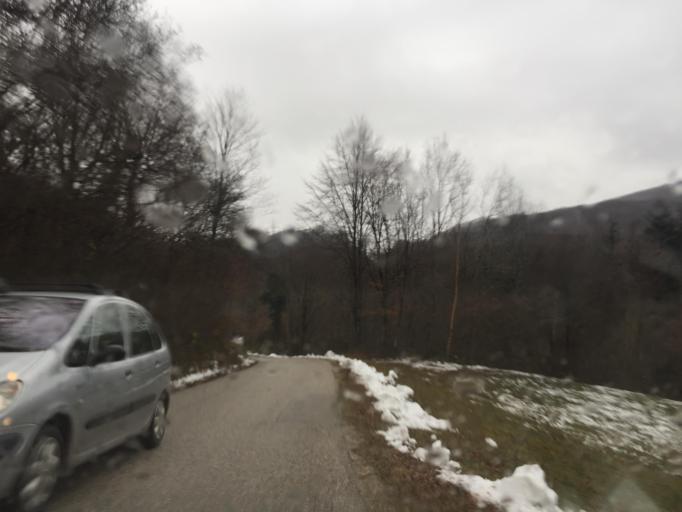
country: SI
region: Kanal
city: Kanal
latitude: 46.0649
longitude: 13.6620
